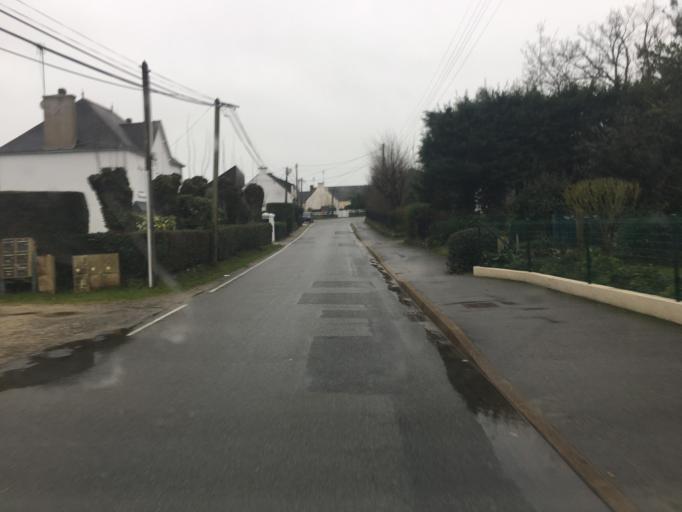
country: FR
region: Brittany
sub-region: Departement du Morbihan
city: Sarzeau
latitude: 47.5001
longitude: -2.6826
